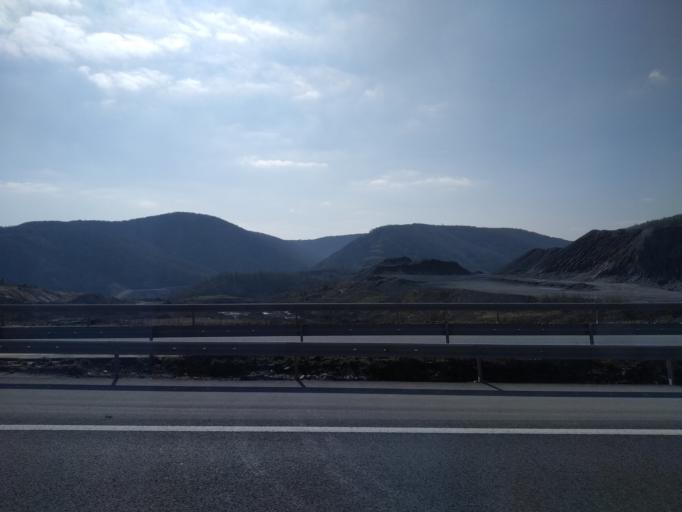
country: TR
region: Istanbul
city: Arikoey
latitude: 41.2236
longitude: 28.9889
